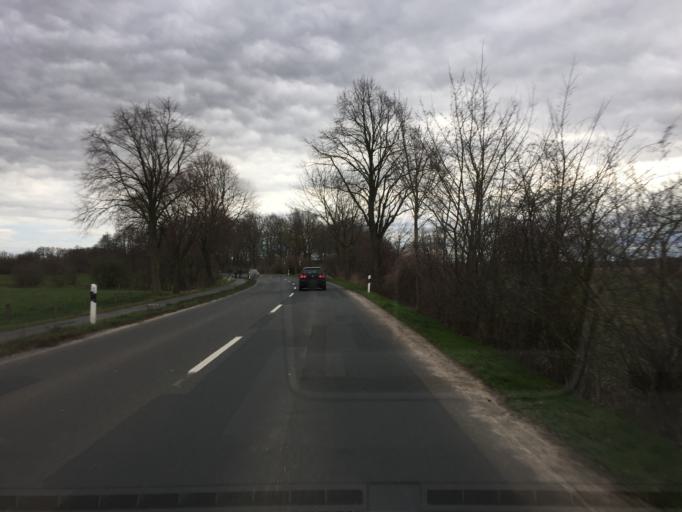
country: DE
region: Lower Saxony
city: Garbsen
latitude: 52.4493
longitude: 9.5263
